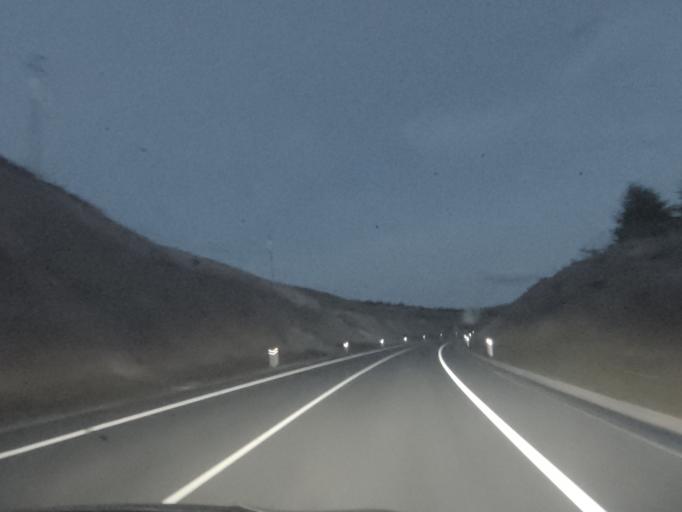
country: PT
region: Braganca
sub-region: Mogadouro
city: Mogadouro
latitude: 41.2640
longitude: -6.7812
